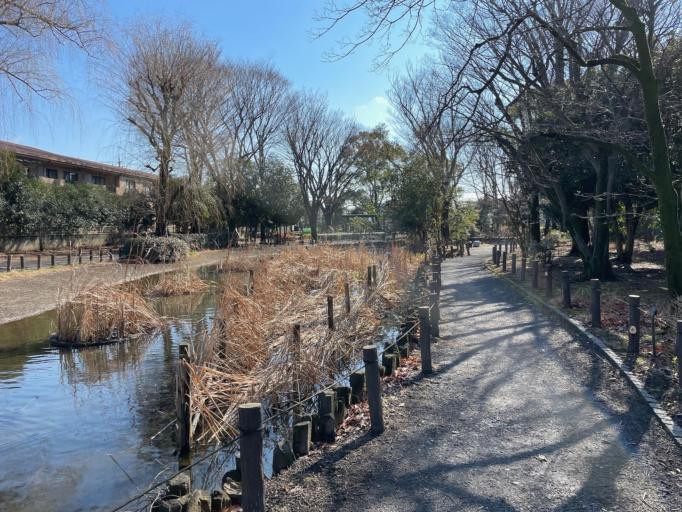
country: JP
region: Tokyo
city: Kokubunji
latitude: 35.6613
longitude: 139.4695
